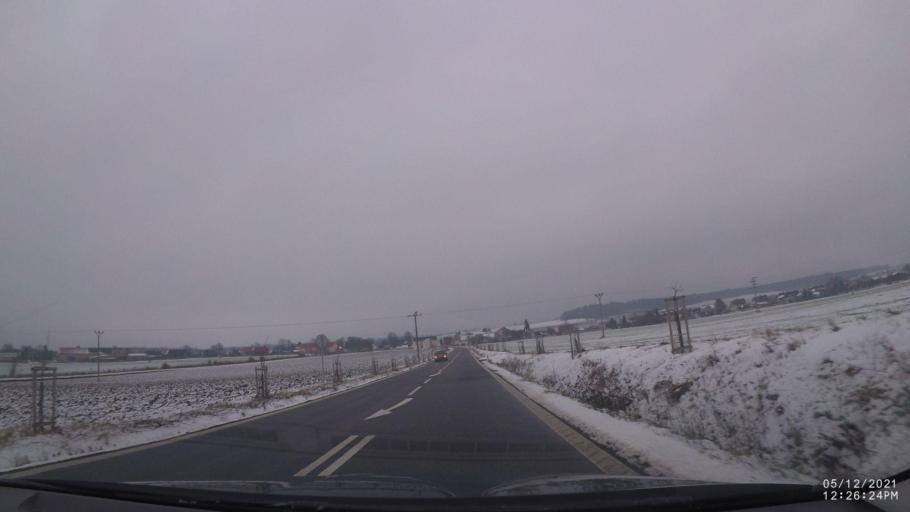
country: CZ
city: Nove Mesto nad Metuji
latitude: 50.3301
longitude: 16.1020
